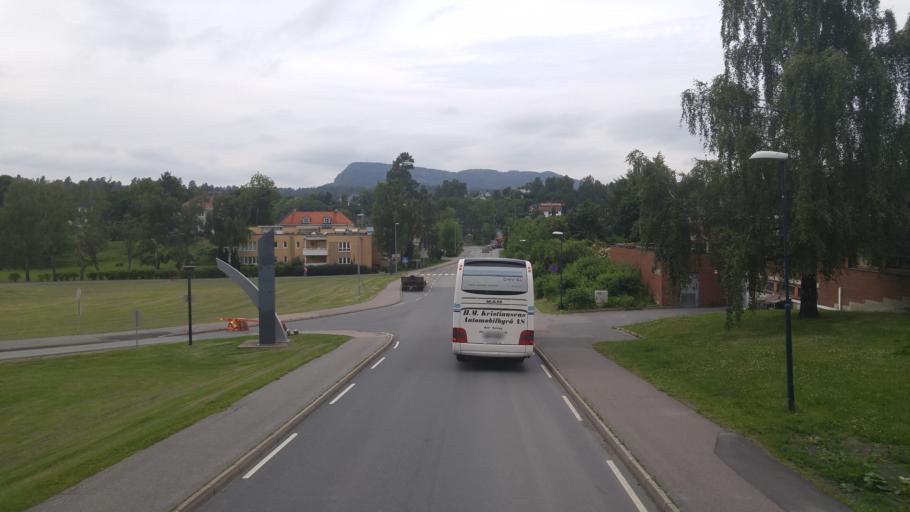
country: NO
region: Akershus
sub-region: Baerum
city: Sandvika
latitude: 59.8913
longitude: 10.5574
